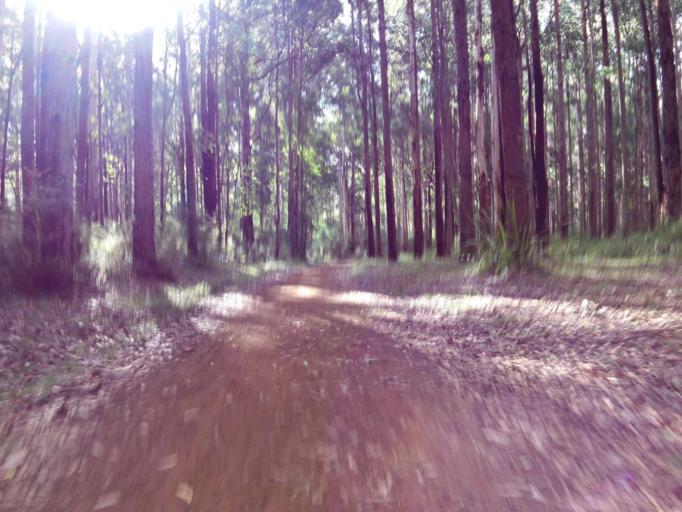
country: AU
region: Victoria
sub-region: Yarra Ranges
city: Mount Dandenong
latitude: -37.8275
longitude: 145.3913
